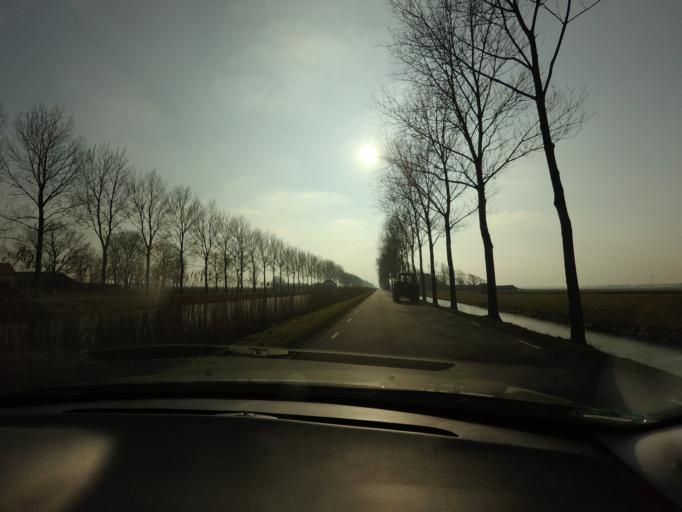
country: NL
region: North Holland
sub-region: Gemeente Alkmaar
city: Alkmaar
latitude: 52.6069
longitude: 4.7917
